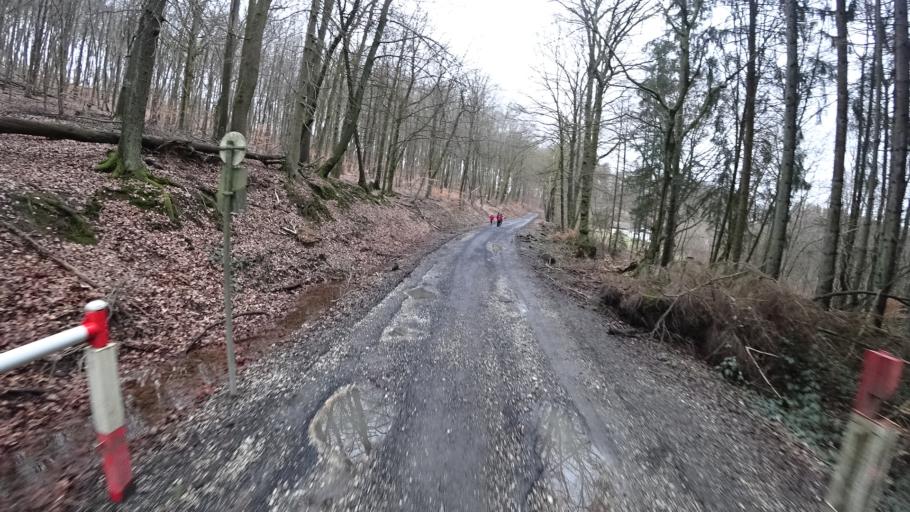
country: DE
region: Rheinland-Pfalz
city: Hilgert
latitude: 50.4299
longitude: 7.6970
